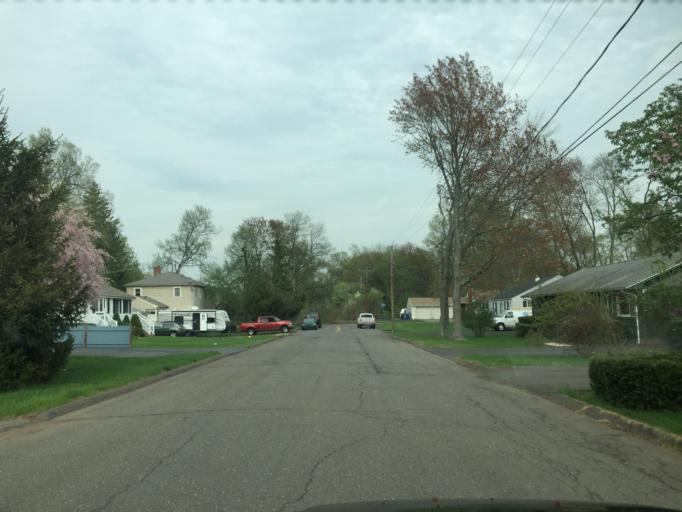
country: US
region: Connecticut
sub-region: Hartford County
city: Newington
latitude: 41.6901
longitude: -72.7424
